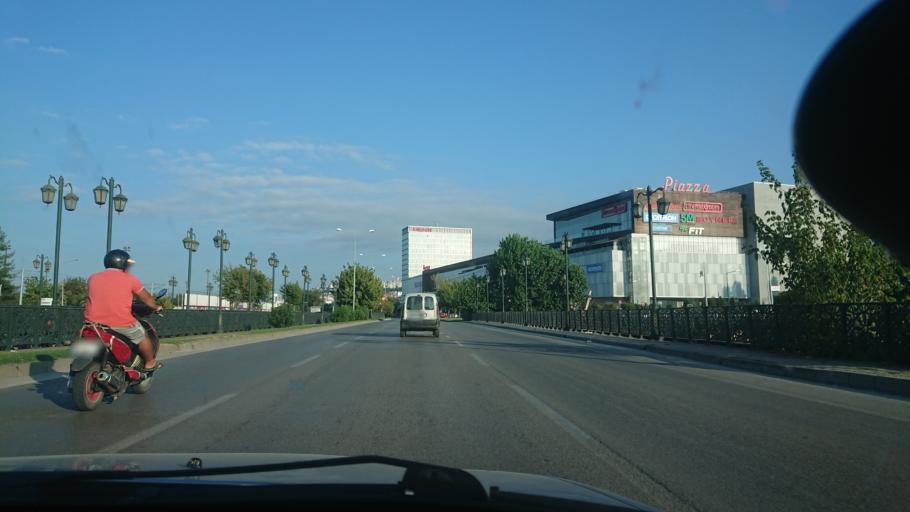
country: TR
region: Samsun
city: Samsun
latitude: 41.2789
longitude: 36.3514
